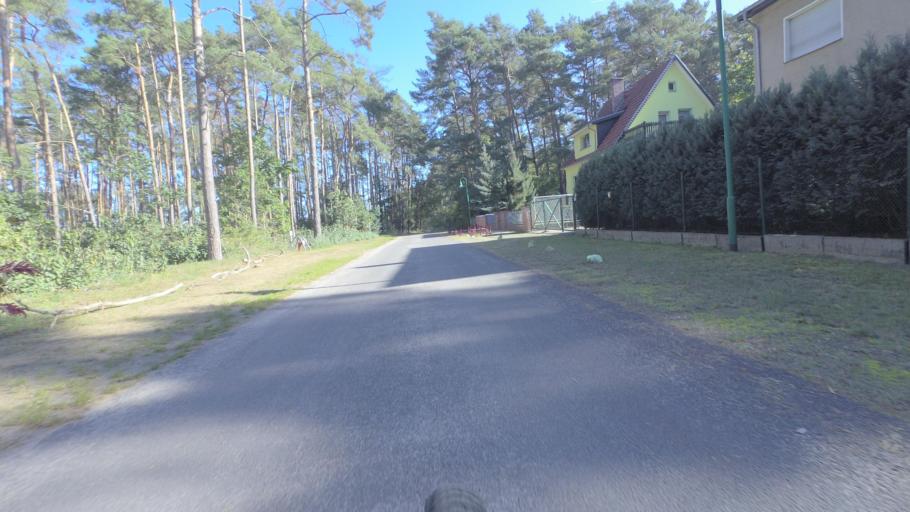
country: DE
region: Brandenburg
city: Am Mellensee
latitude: 52.1931
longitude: 13.3968
